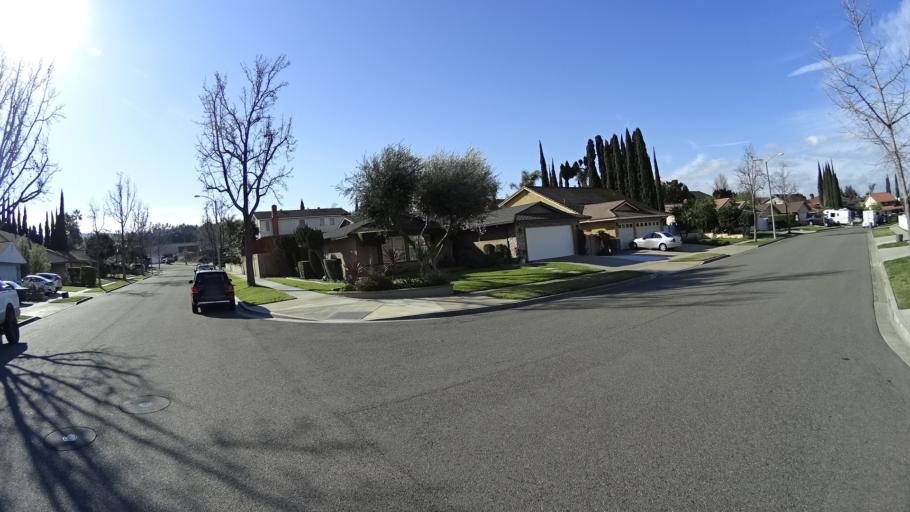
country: US
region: California
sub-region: Orange County
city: Villa Park
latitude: 33.8486
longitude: -117.8217
